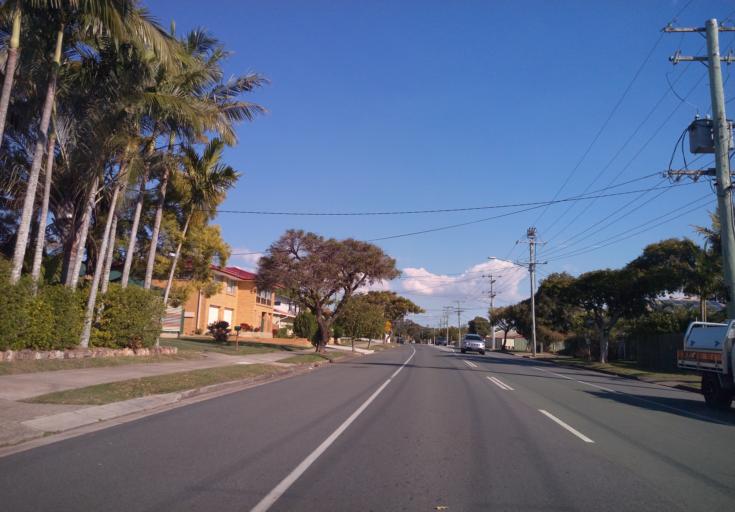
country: AU
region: Queensland
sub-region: Redland
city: Wellington Point
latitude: -27.5163
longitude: 153.2122
